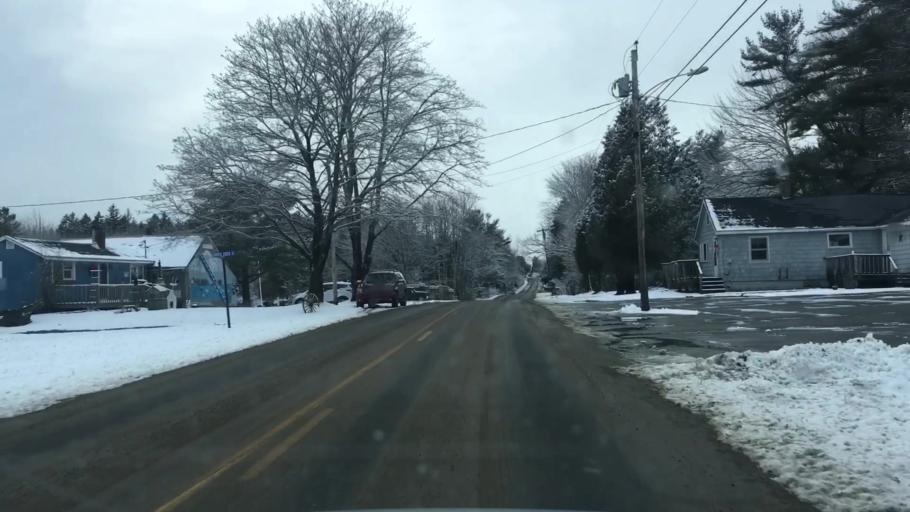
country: US
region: Maine
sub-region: Knox County
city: Owls Head
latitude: 44.0640
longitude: -69.0812
